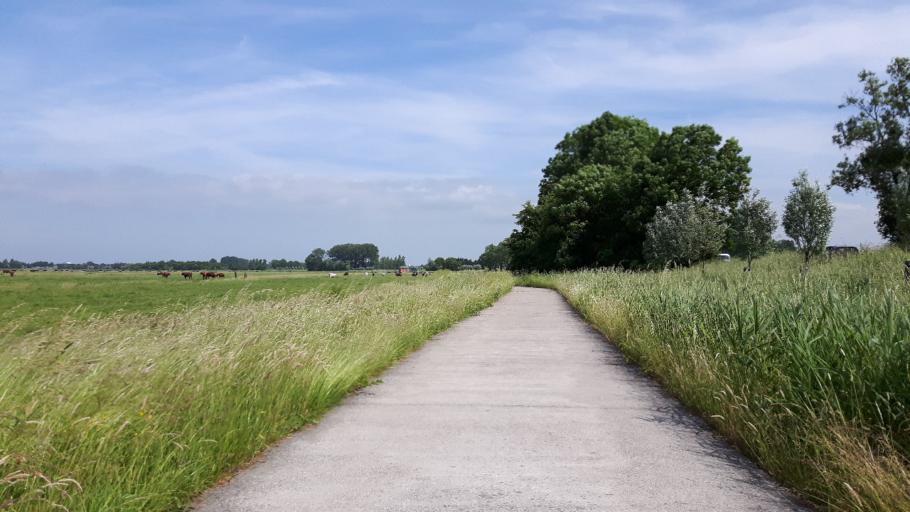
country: NL
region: North Holland
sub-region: Gemeente Uithoorn
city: Uithoorn
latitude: 52.2283
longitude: 4.7897
